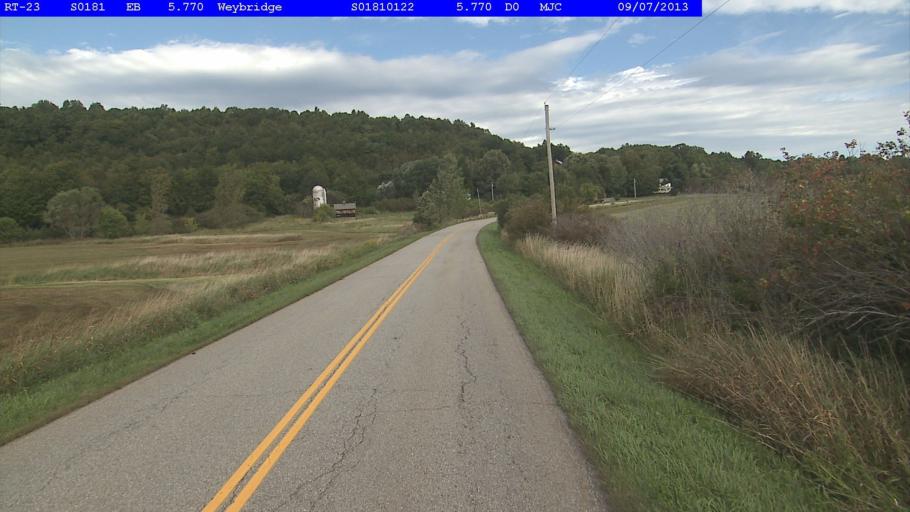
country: US
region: Vermont
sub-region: Addison County
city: Vergennes
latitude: 44.0735
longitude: -73.2532
